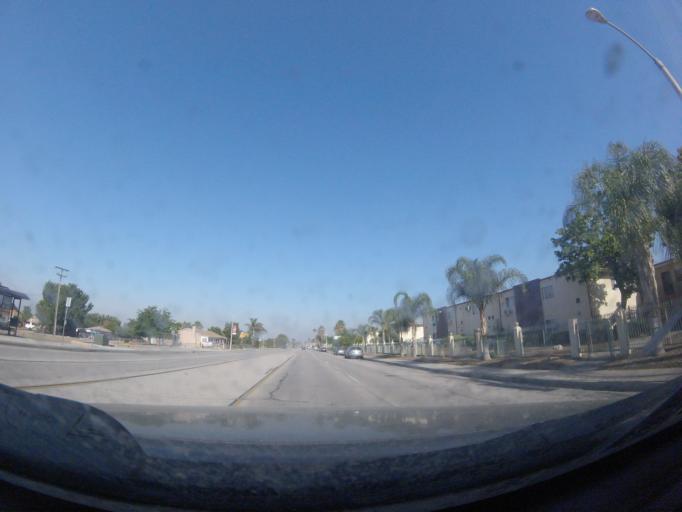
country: US
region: California
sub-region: San Bernardino County
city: Highland
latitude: 34.1213
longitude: -117.2130
